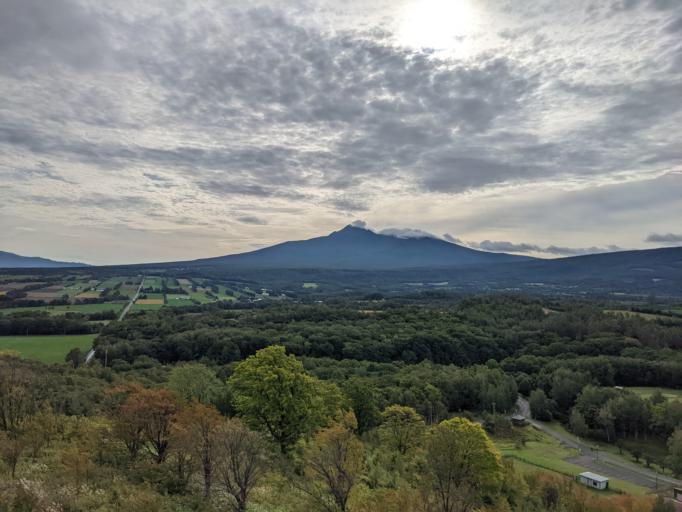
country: JP
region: Hokkaido
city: Abashiri
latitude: 43.7960
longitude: 144.5759
